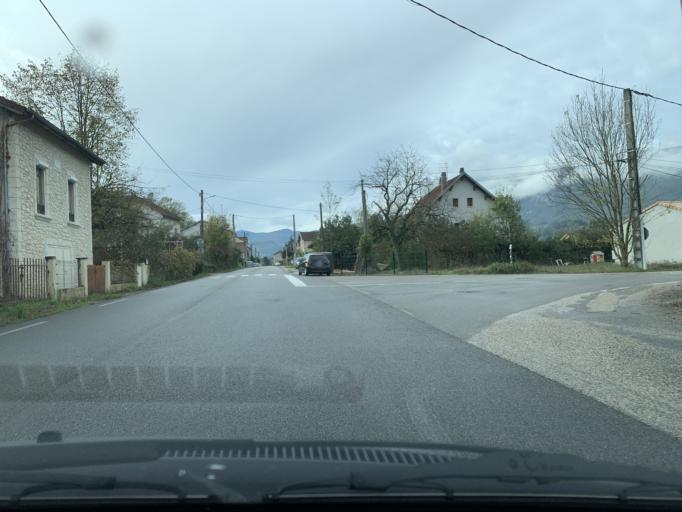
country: FR
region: Rhone-Alpes
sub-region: Departement de la Drome
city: Saint-Jean-en-Royans
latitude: 45.0242
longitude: 5.2964
